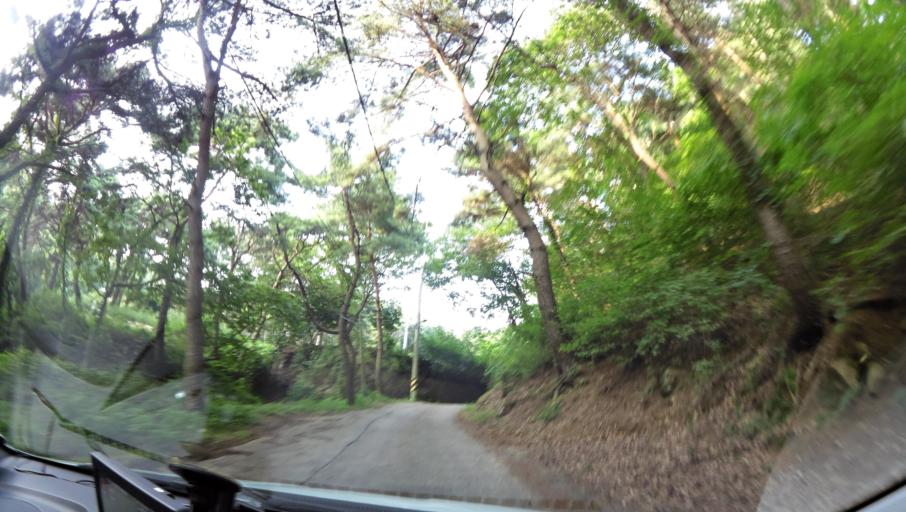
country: KR
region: Daegu
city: Daegu
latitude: 35.9869
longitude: 128.6544
